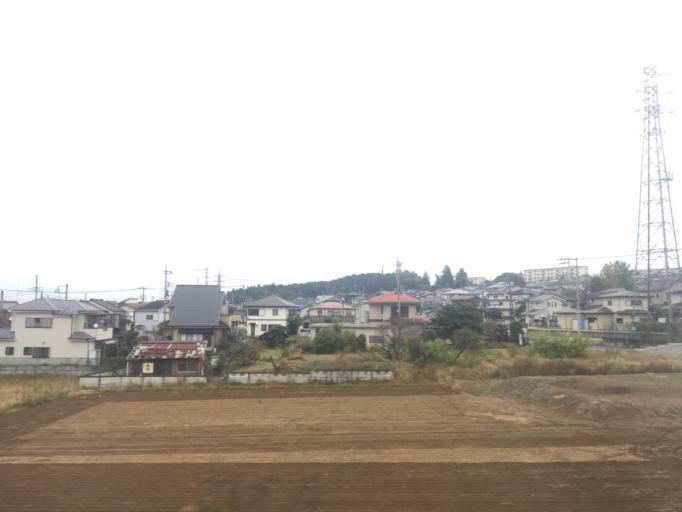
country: JP
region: Saitama
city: Hanno
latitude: 35.8895
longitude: 139.3418
